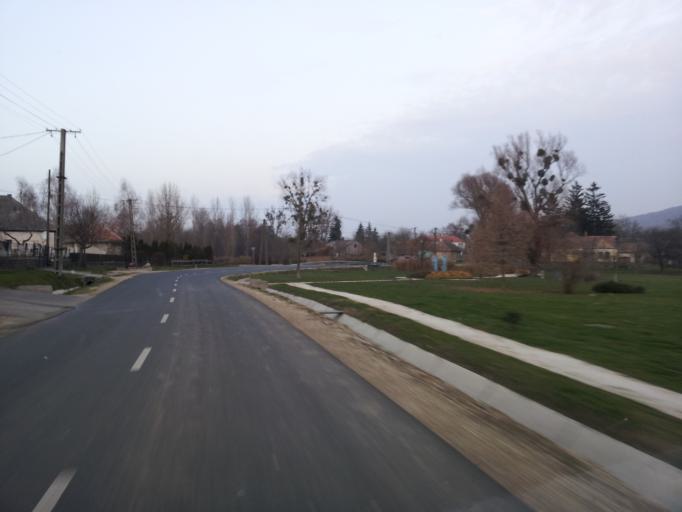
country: HU
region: Zala
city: Zalaszentgrot
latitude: 46.8947
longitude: 17.1522
